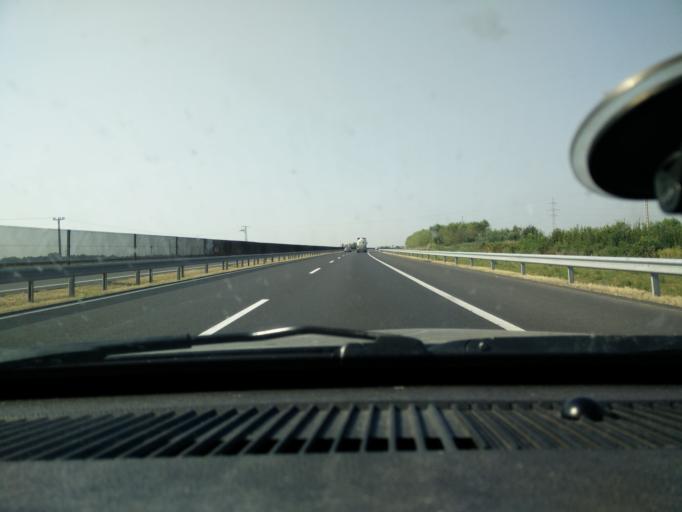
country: HU
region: Fejer
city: Ivancsa
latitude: 47.1983
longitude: 18.8167
